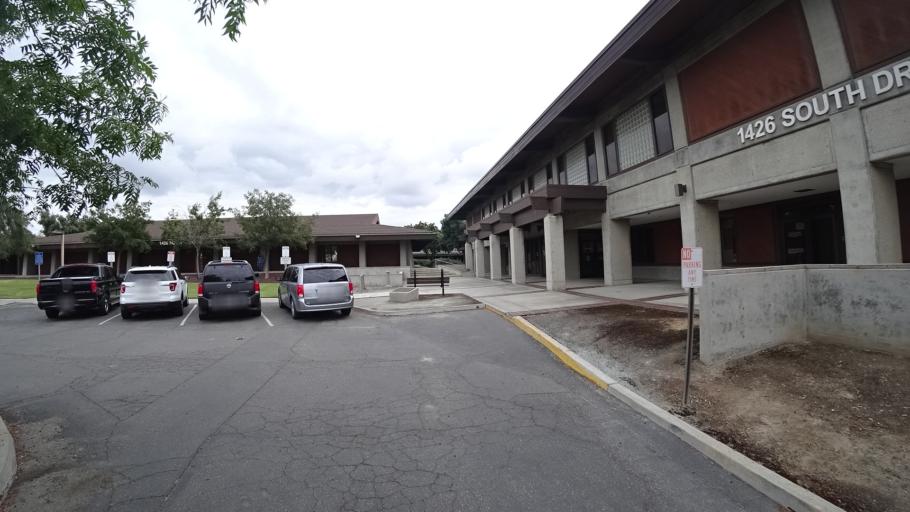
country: US
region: California
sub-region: Kings County
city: Hanford
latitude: 36.3298
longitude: -119.6680
